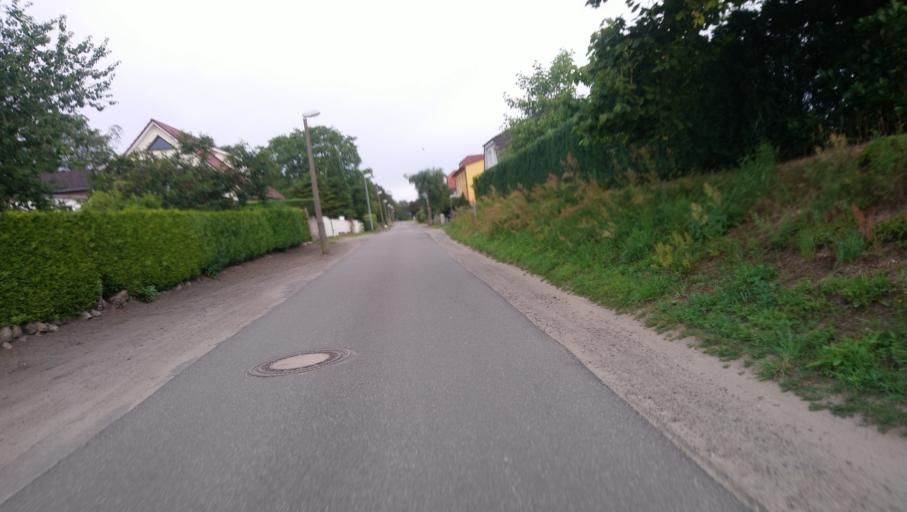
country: DE
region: Mecklenburg-Vorpommern
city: Papendorf
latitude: 54.0660
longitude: 12.1068
